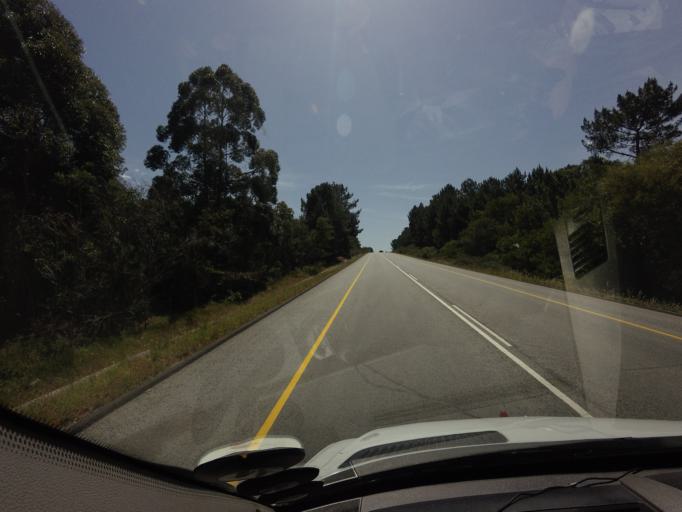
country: ZA
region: Western Cape
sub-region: Overberg District Municipality
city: Hermanus
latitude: -34.3028
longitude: 19.1366
